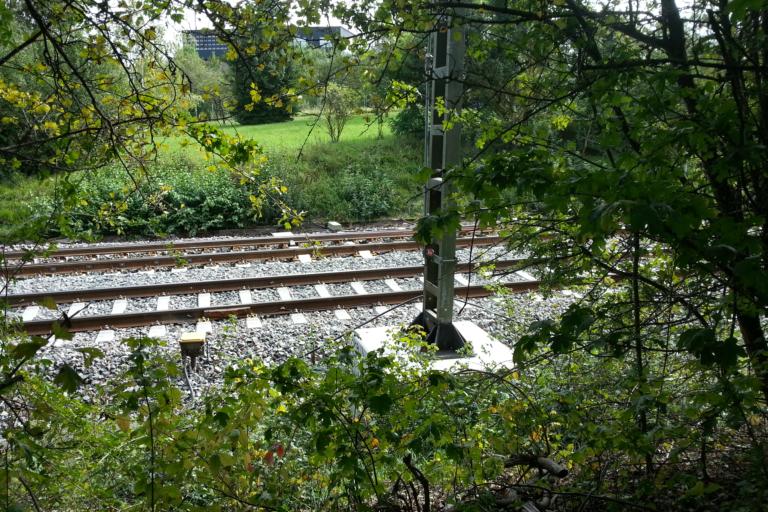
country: DE
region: Baden-Wuerttemberg
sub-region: Regierungsbezirk Stuttgart
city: Gartringen
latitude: 48.6366
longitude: 8.9051
